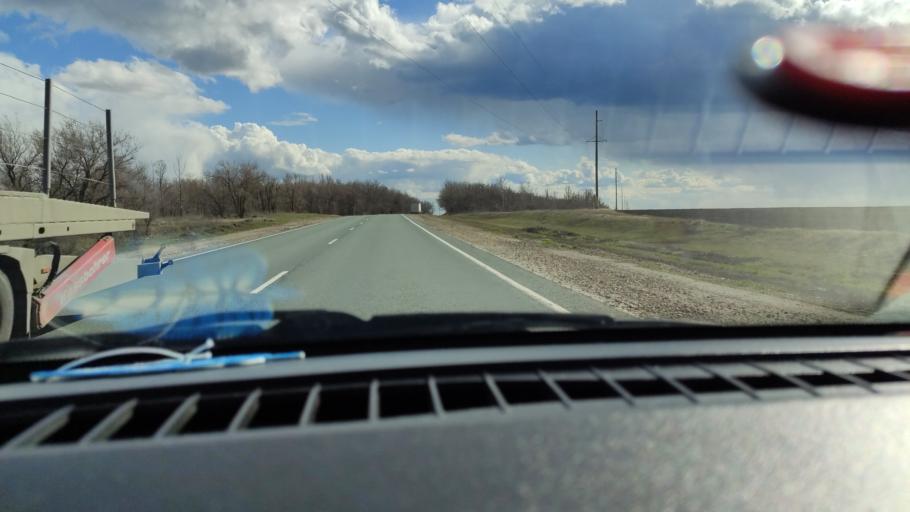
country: RU
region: Saratov
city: Alekseyevka
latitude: 52.2719
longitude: 47.9297
